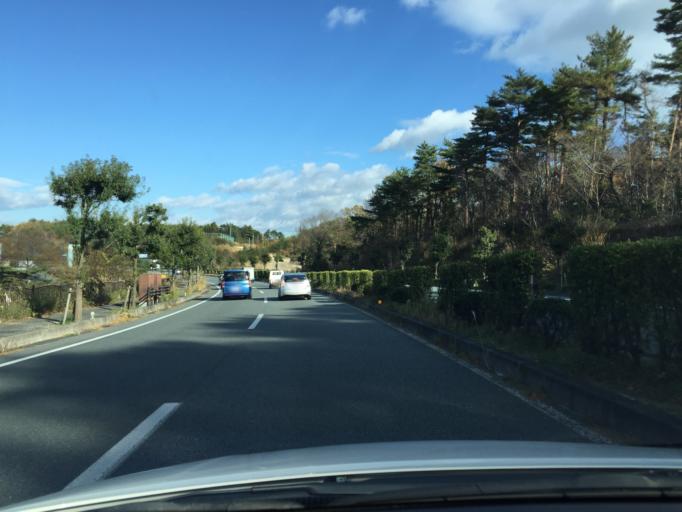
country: JP
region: Fukushima
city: Iwaki
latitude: 37.2418
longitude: 141.0003
